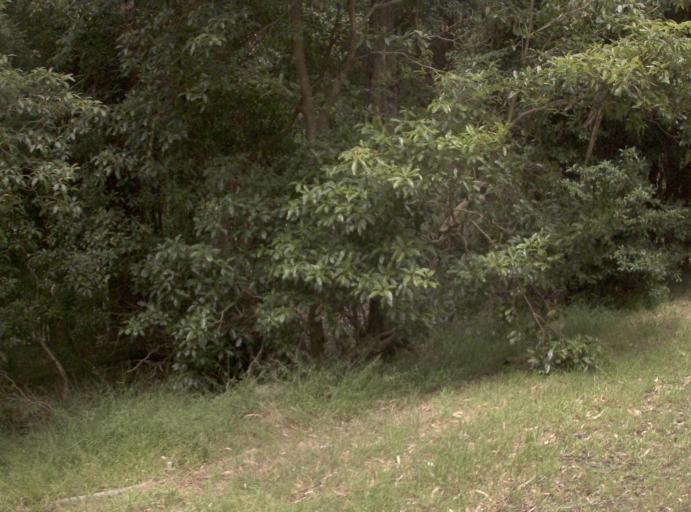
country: AU
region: Victoria
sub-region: Latrobe
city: Traralgon
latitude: -38.4321
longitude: 146.7371
